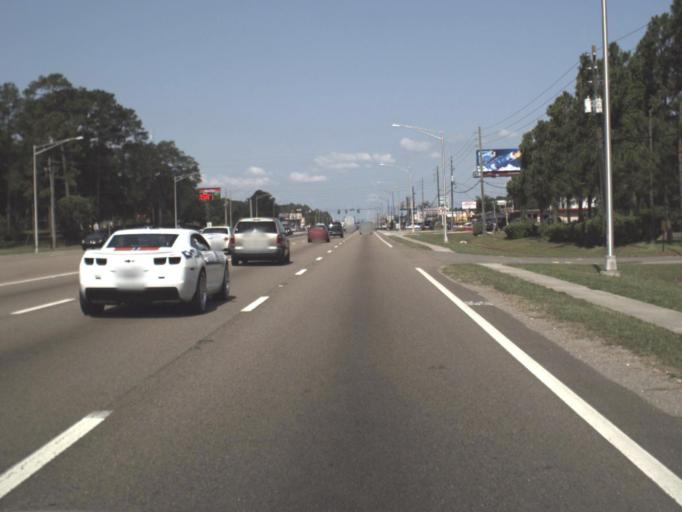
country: US
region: Florida
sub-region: Duval County
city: Jacksonville
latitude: 30.2869
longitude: -81.5411
